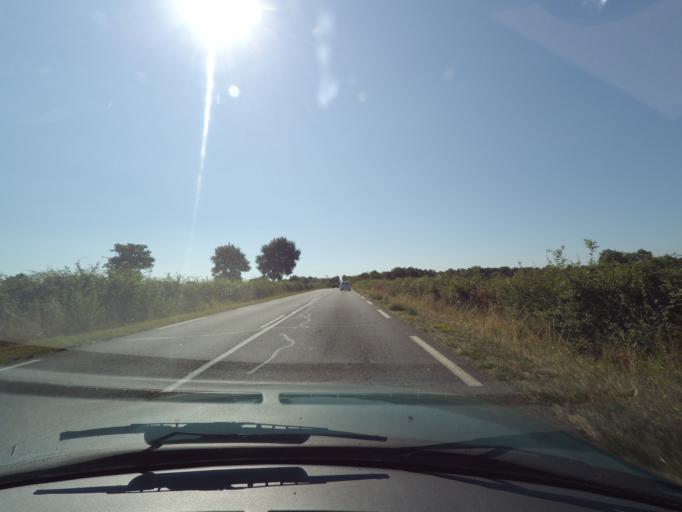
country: FR
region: Limousin
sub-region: Departement de la Haute-Vienne
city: Peyrat-de-Bellac
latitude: 46.1401
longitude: 0.9785
